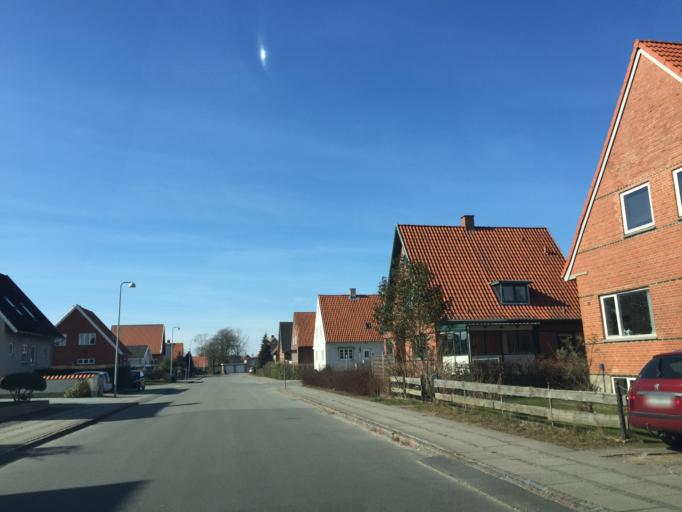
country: DK
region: South Denmark
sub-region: Odense Kommune
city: Odense
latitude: 55.3895
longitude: 10.4215
